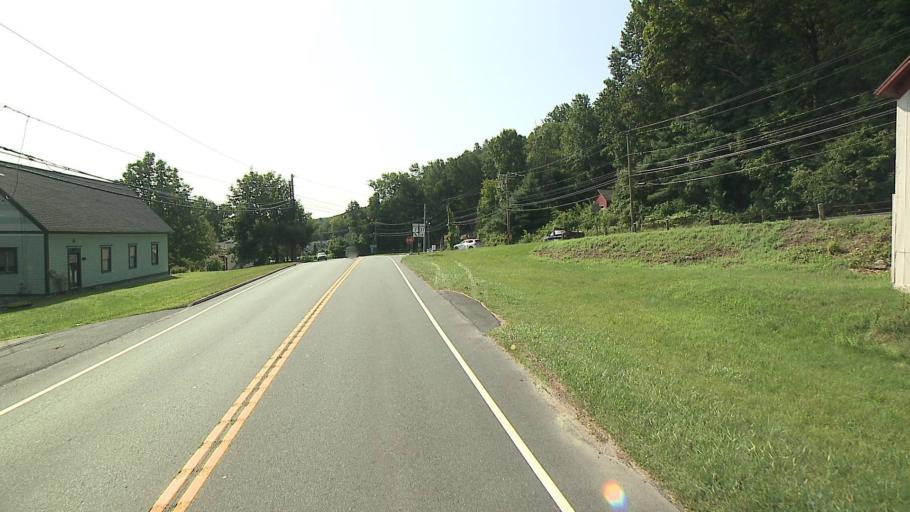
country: US
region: Connecticut
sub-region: Fairfield County
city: Sherman
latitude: 41.5955
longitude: -73.4574
